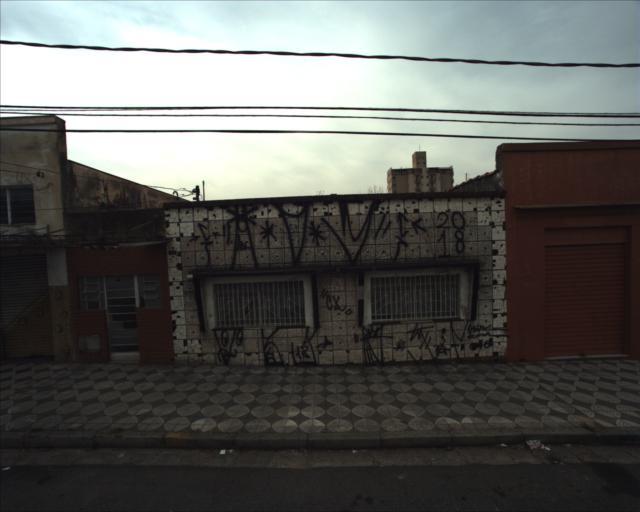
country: BR
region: Sao Paulo
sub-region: Sorocaba
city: Sorocaba
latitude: -23.4928
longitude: -47.4649
